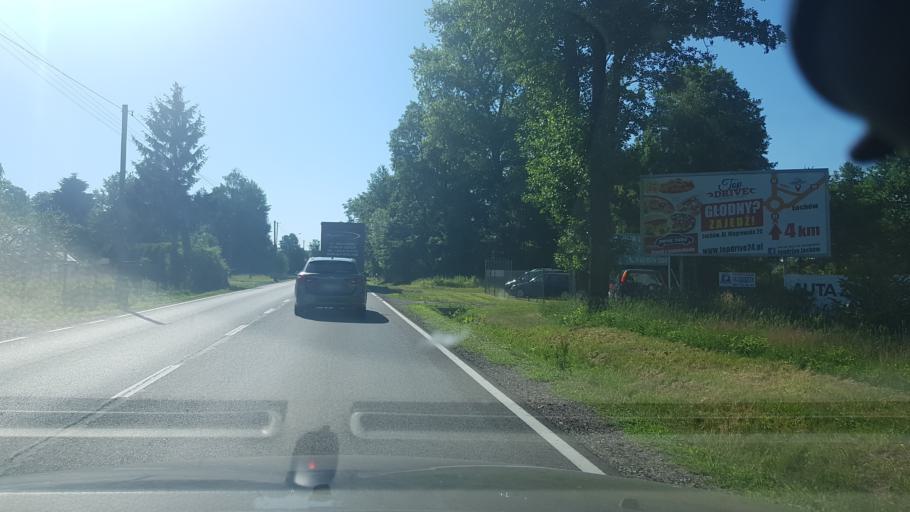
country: PL
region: Masovian Voivodeship
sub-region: Powiat wegrowski
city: Lochow
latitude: 52.5459
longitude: 21.6365
